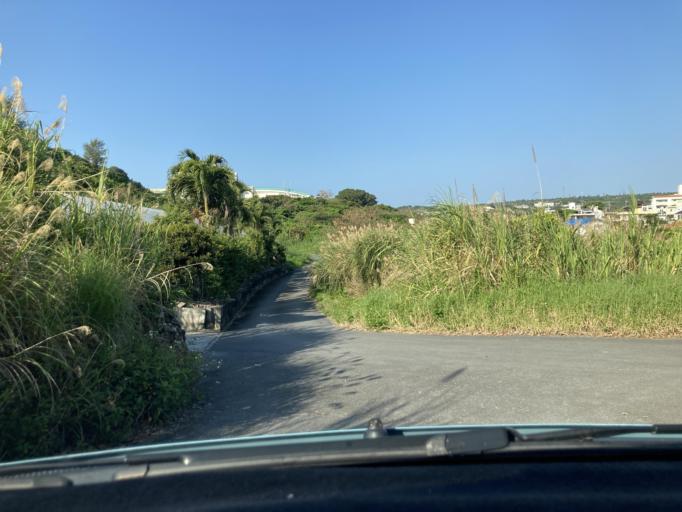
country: JP
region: Okinawa
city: Itoman
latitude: 26.1205
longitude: 127.7464
